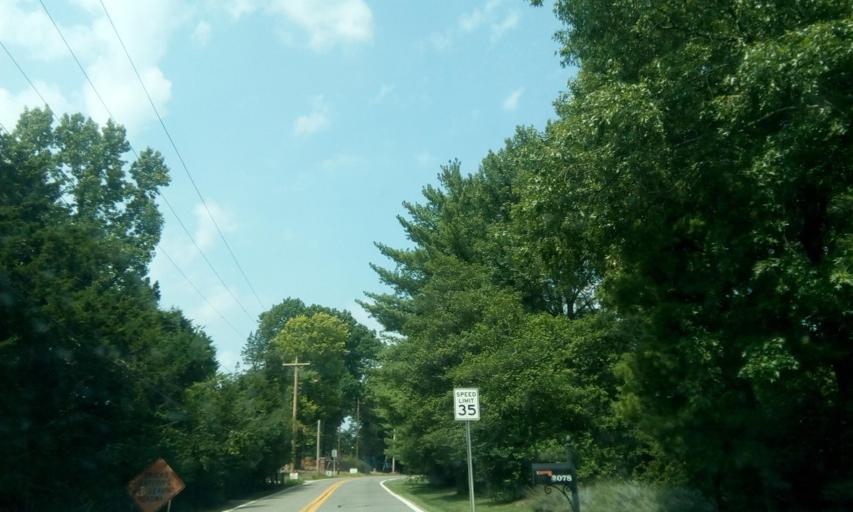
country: US
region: Missouri
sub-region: Saint Louis County
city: Town and Country
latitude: 38.5995
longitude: -90.4800
